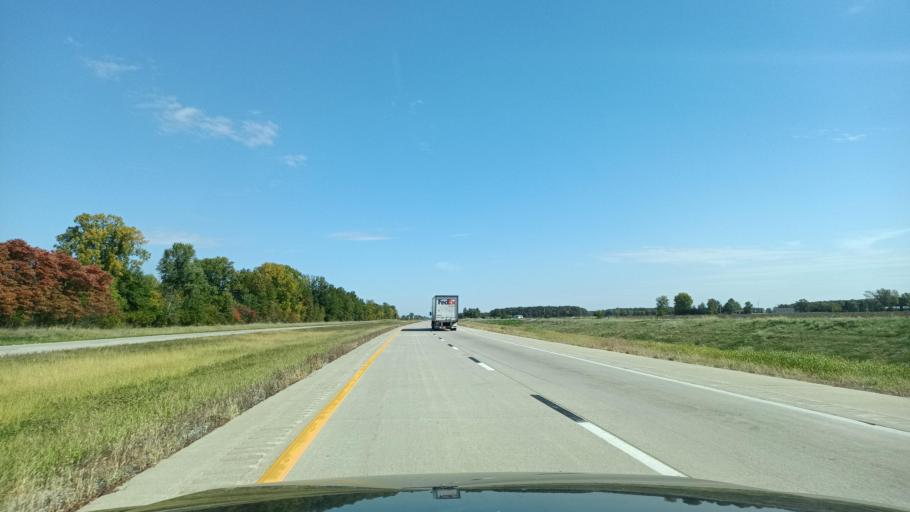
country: US
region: Ohio
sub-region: Paulding County
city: Antwerp
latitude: 41.1956
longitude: -84.6821
